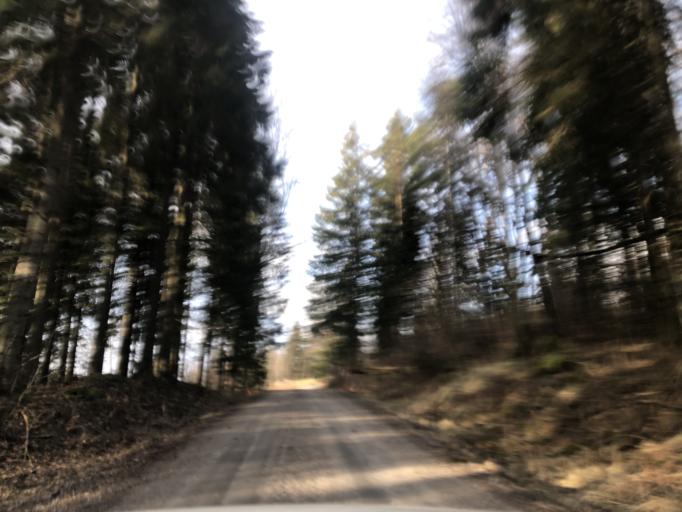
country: SE
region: Vaestra Goetaland
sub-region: Ulricehamns Kommun
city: Ulricehamn
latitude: 57.8157
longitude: 13.3599
